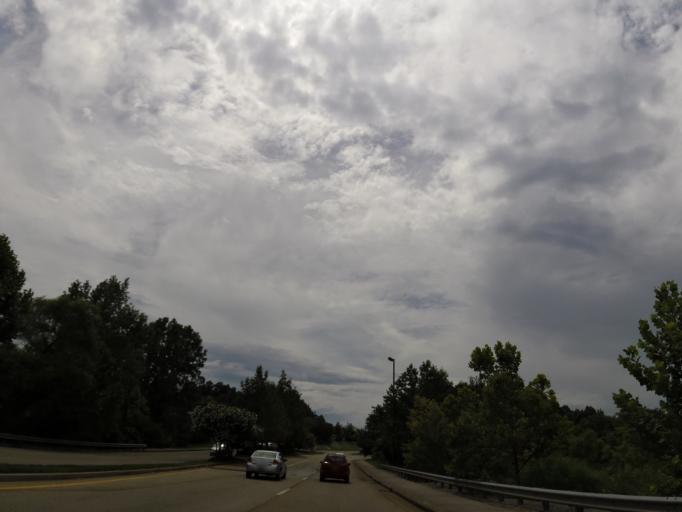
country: US
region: Tennessee
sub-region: Knox County
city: Farragut
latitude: 35.9005
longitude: -84.1422
